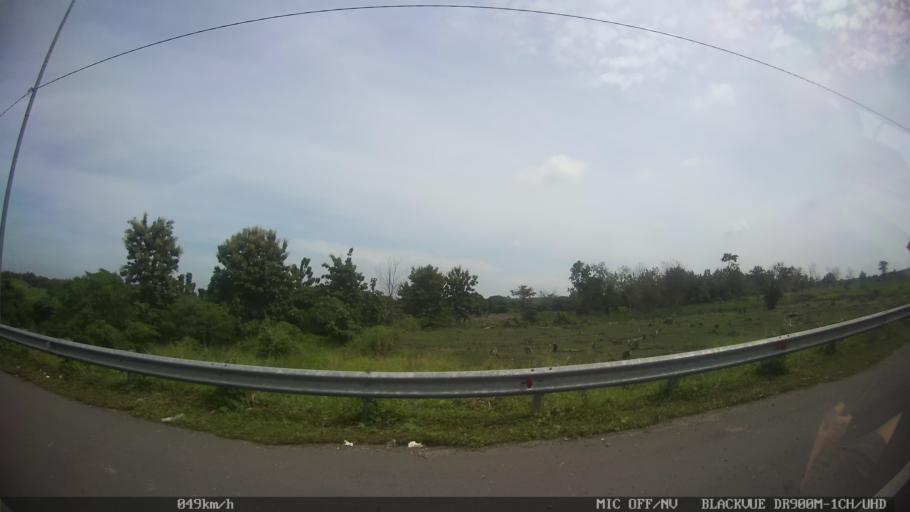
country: ID
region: North Sumatra
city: Medan
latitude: 3.6380
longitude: 98.6374
